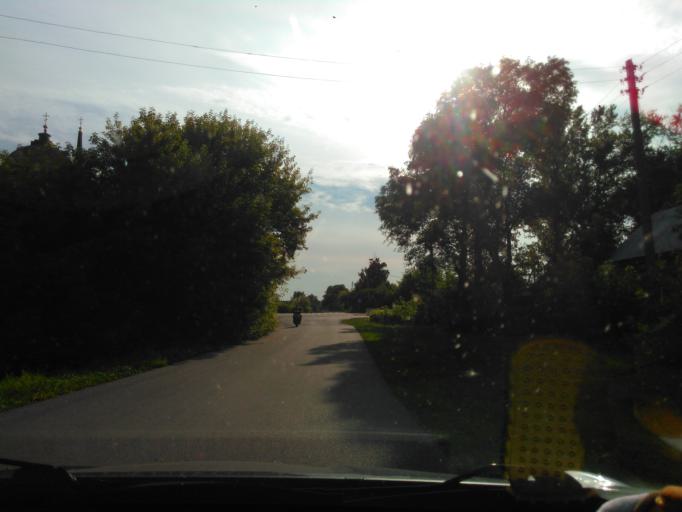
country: RU
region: Penza
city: Lermontovo
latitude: 52.9927
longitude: 43.6596
